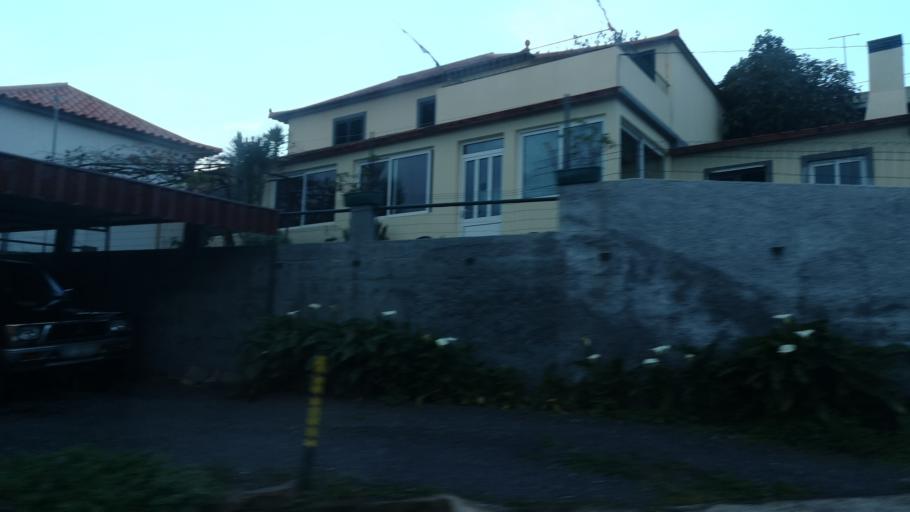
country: PT
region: Madeira
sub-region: Santa Cruz
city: Santa Cruz
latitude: 32.6729
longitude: -16.8182
